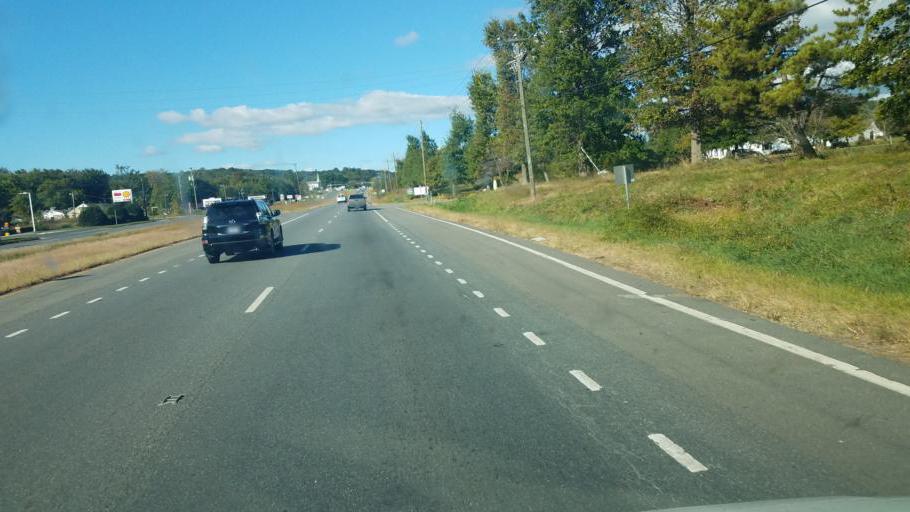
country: US
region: Virginia
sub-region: Fauquier County
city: New Baltimore
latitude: 38.7684
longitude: -77.7083
